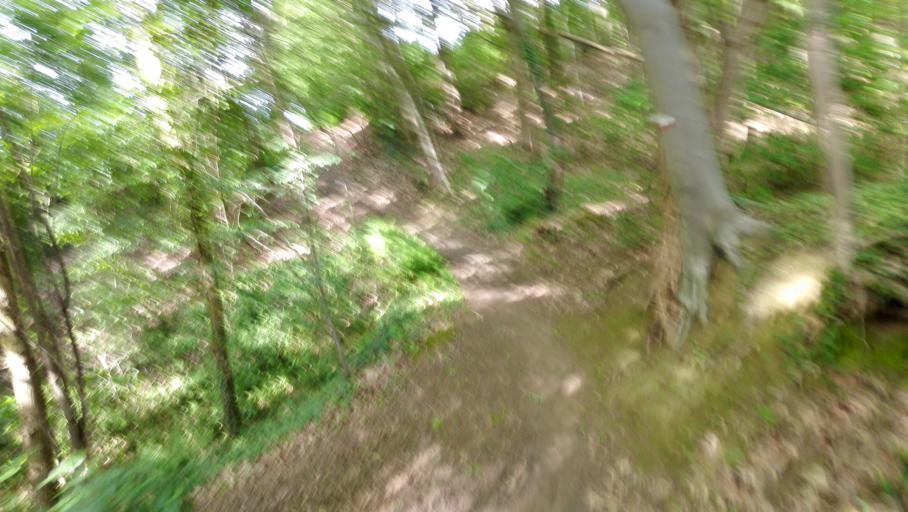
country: BE
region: Flanders
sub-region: Provincie Vlaams-Brabant
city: Holsbeek
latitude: 50.8795
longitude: 4.7600
